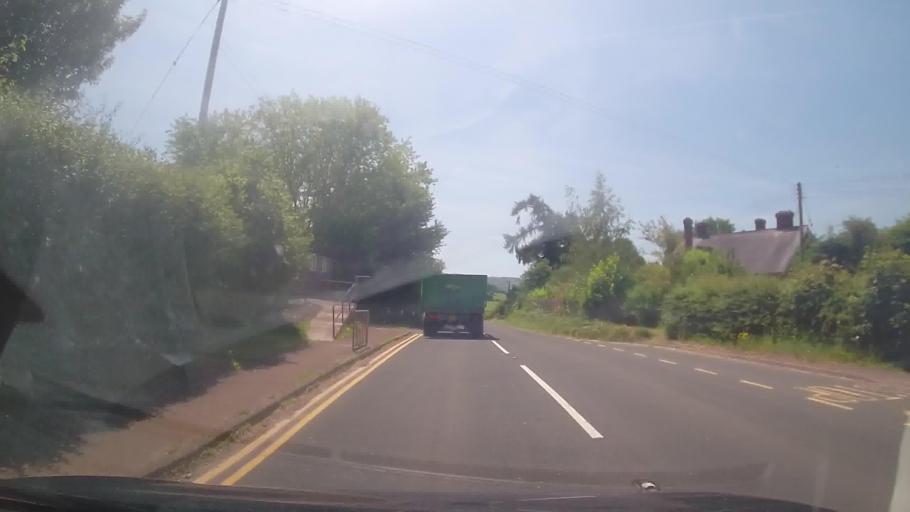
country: GB
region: England
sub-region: Herefordshire
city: Pencoyd
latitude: 51.9141
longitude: -2.7351
